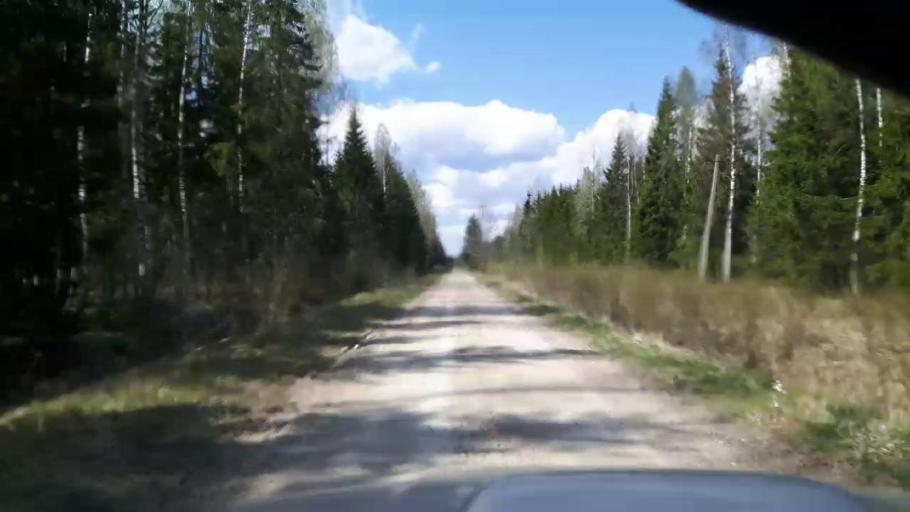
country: EE
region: Paernumaa
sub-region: Tootsi vald
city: Tootsi
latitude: 58.4437
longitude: 24.9190
